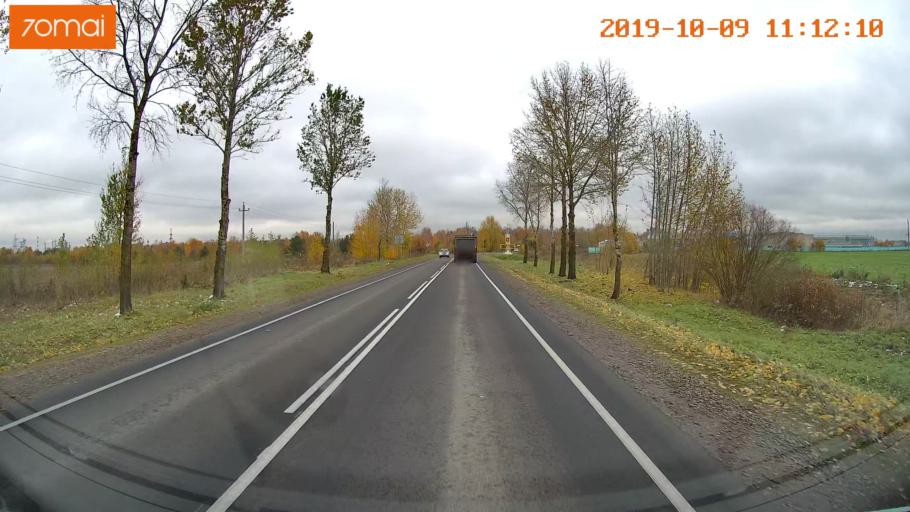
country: RU
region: Vologda
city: Vologda
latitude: 59.1751
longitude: 39.8272
